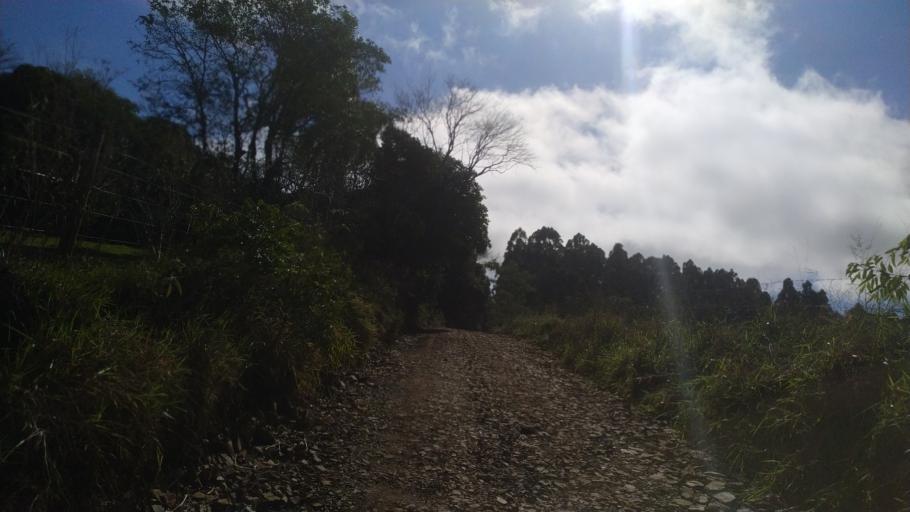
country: BR
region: Santa Catarina
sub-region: Chapeco
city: Chapeco
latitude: -27.1619
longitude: -52.5973
